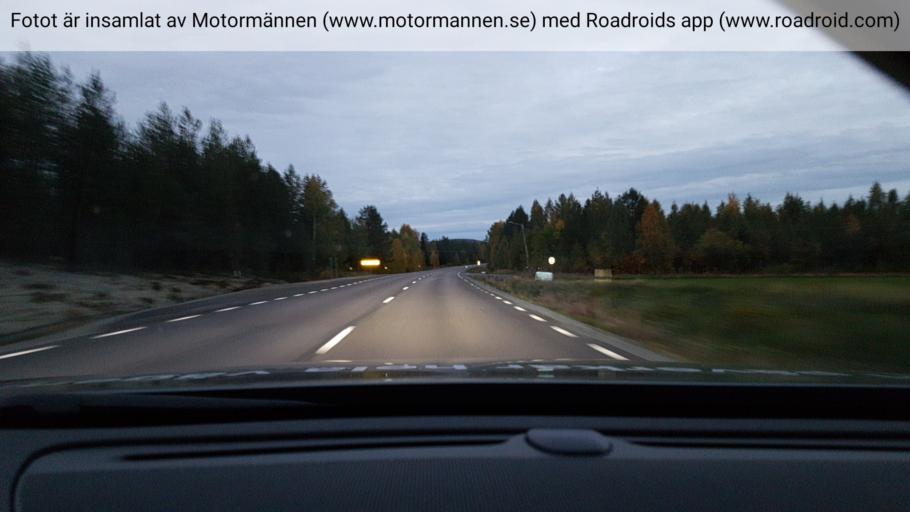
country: SE
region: Norrbotten
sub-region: Alvsbyns Kommun
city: AElvsbyn
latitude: 65.7347
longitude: 20.9764
